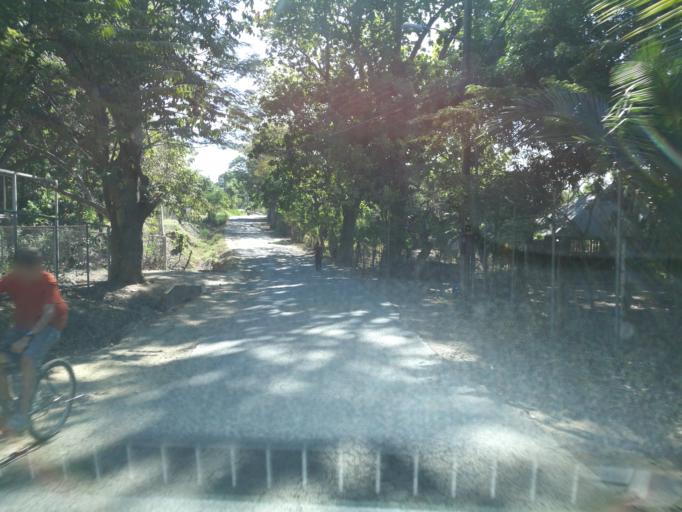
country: CR
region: Guanacaste
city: Juntas
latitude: 10.0995
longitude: -84.9926
